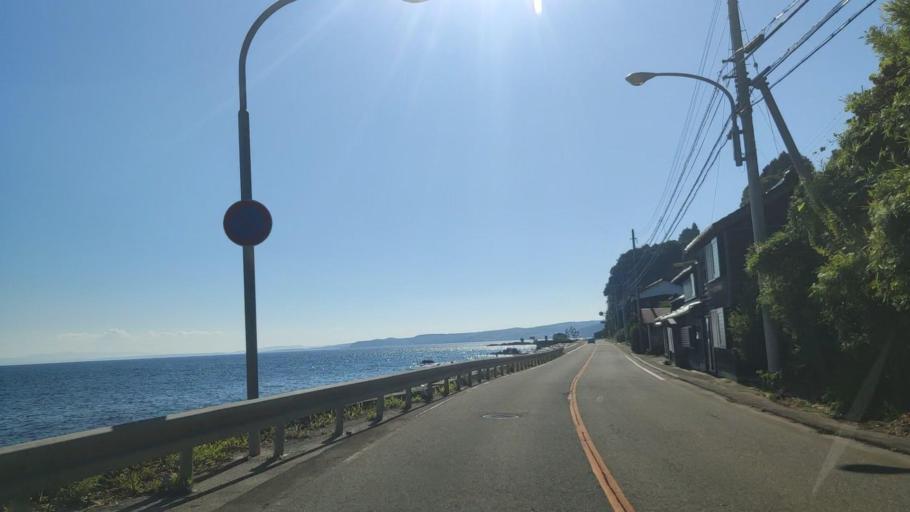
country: JP
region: Ishikawa
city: Nanao
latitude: 37.2940
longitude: 137.1357
